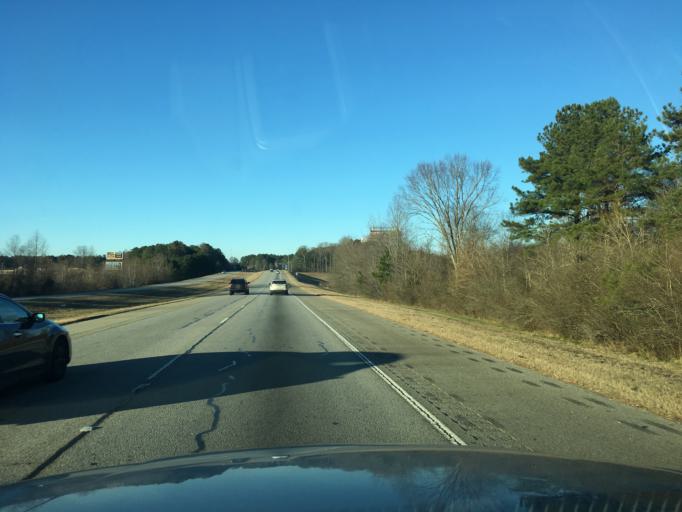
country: US
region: Georgia
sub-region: Carroll County
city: Carrollton
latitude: 33.5868
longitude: -85.0414
